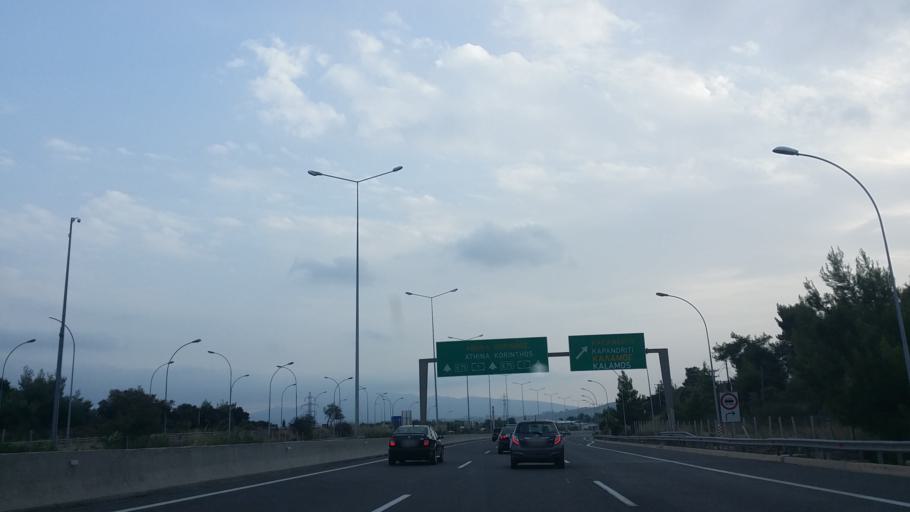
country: GR
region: Attica
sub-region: Nomarchia Anatolikis Attikis
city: Polydendri
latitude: 38.2073
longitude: 23.8550
